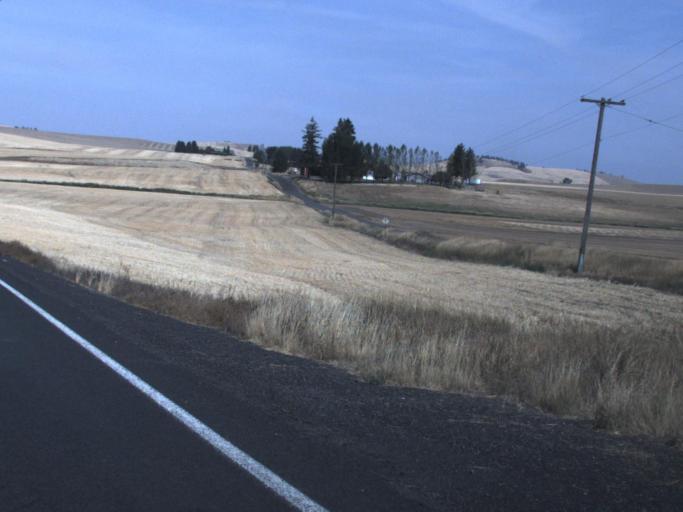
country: US
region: Idaho
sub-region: Benewah County
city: Plummer
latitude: 47.3105
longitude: -117.1640
